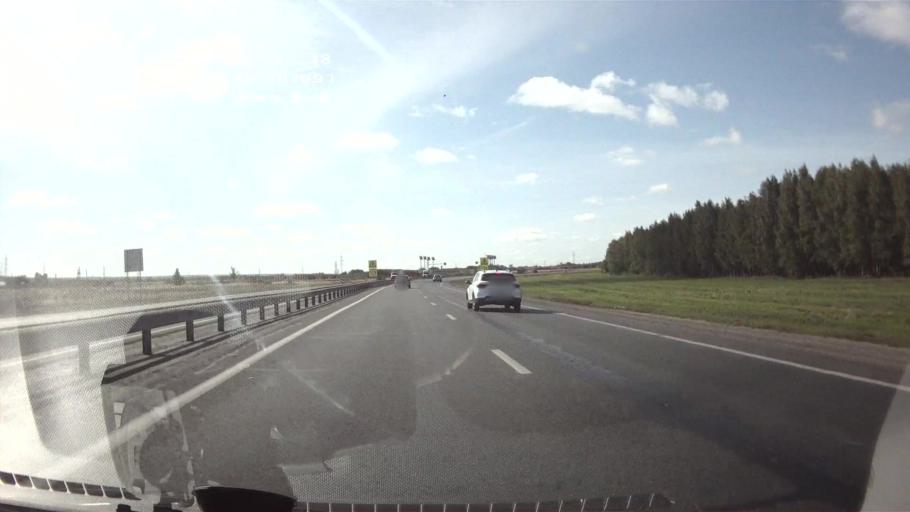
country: RU
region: Ulyanovsk
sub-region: Ulyanovskiy Rayon
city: Ulyanovsk
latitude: 54.2725
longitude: 48.2610
